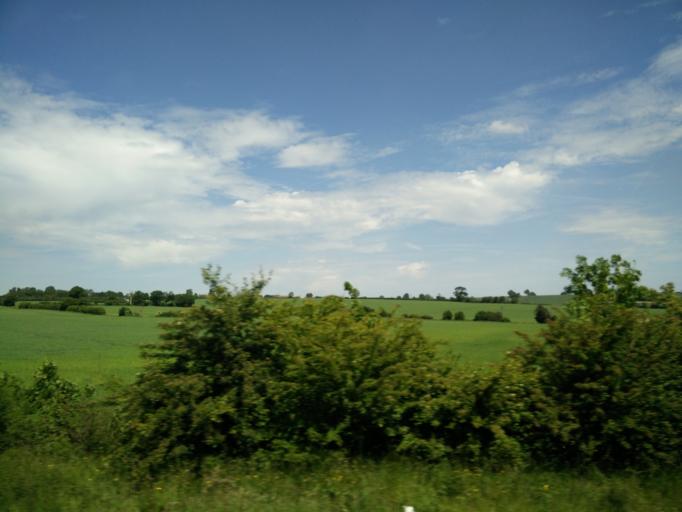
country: GB
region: England
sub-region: Hertfordshire
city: Flamstead
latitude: 51.8211
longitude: -0.4153
